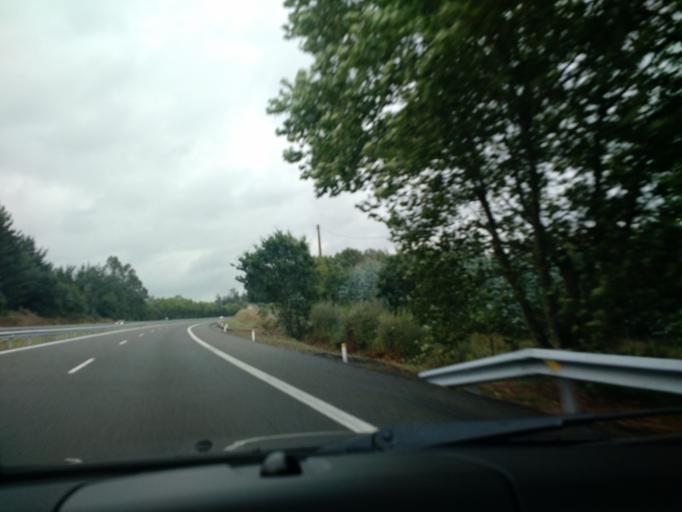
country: ES
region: Galicia
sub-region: Provincia da Coruna
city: Oroso
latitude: 43.0087
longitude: -8.4194
